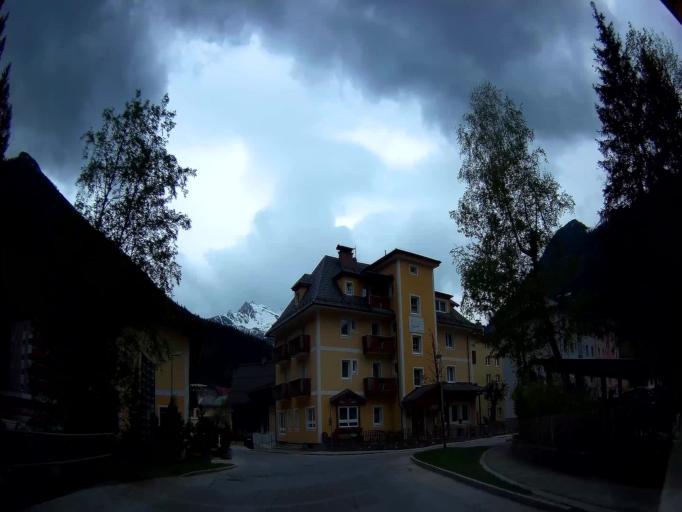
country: AT
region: Salzburg
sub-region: Politischer Bezirk Sankt Johann im Pongau
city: Bad Gastein
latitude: 47.1098
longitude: 13.1363
